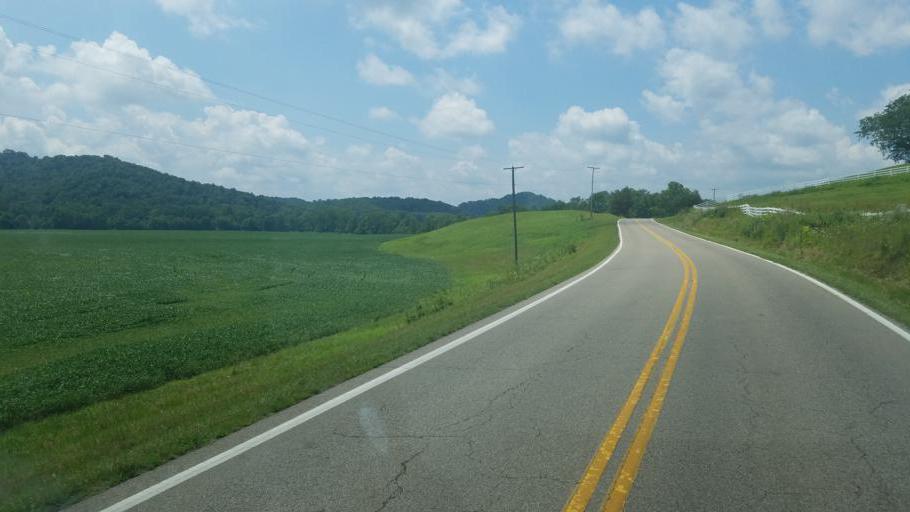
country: US
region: Ohio
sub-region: Ross County
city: Chillicothe
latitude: 39.2894
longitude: -82.7567
